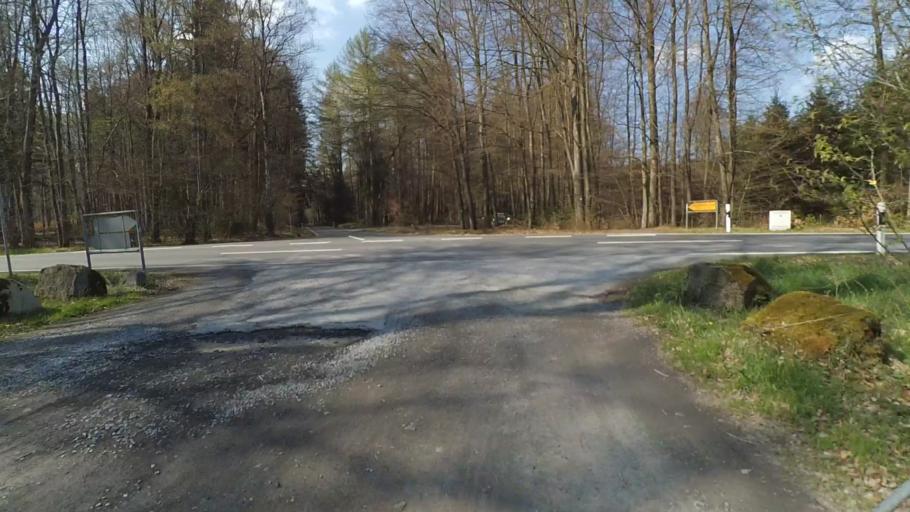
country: DE
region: Rheinland-Pfalz
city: Freilingen
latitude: 50.5809
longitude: 7.8270
